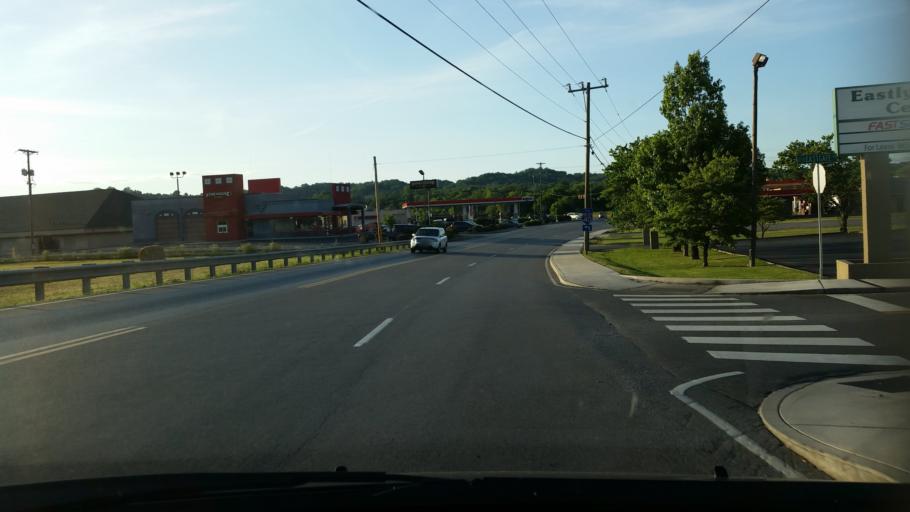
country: US
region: Tennessee
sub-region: Sevier County
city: Sevierville
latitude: 35.8625
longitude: -83.5465
